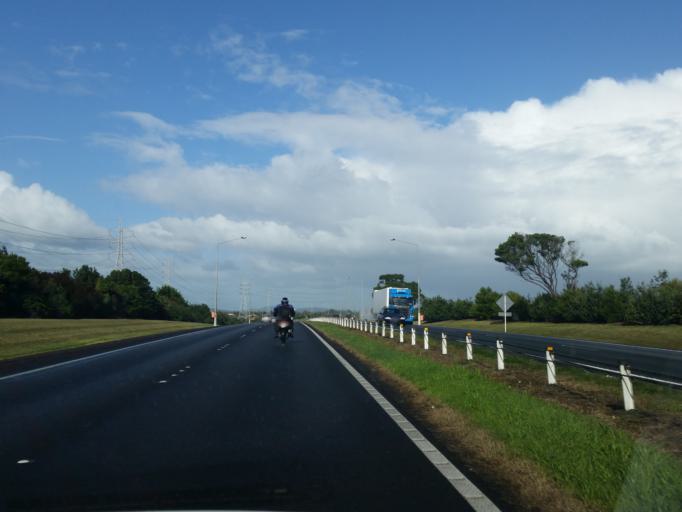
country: NZ
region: Auckland
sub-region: Auckland
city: Takanini
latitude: -37.0537
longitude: 174.9192
